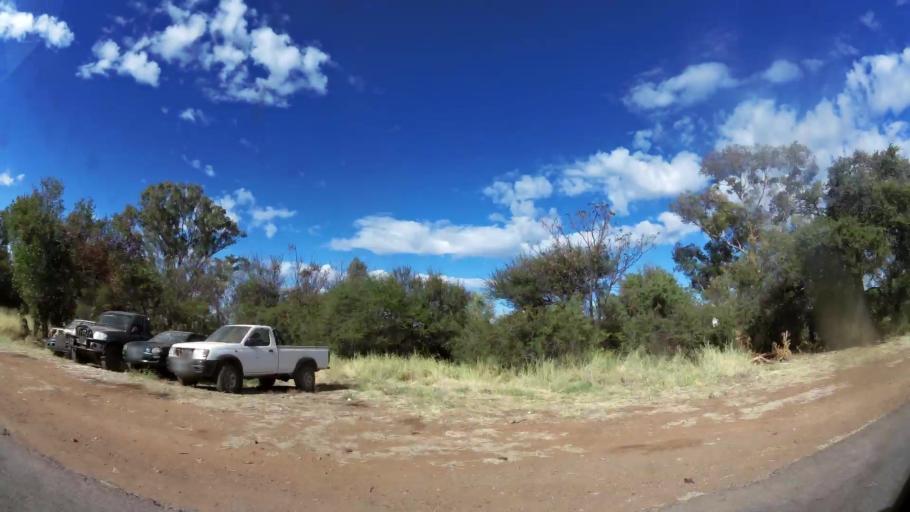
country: ZA
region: Limpopo
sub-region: Waterberg District Municipality
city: Warmbaths
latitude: -24.8815
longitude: 28.2768
